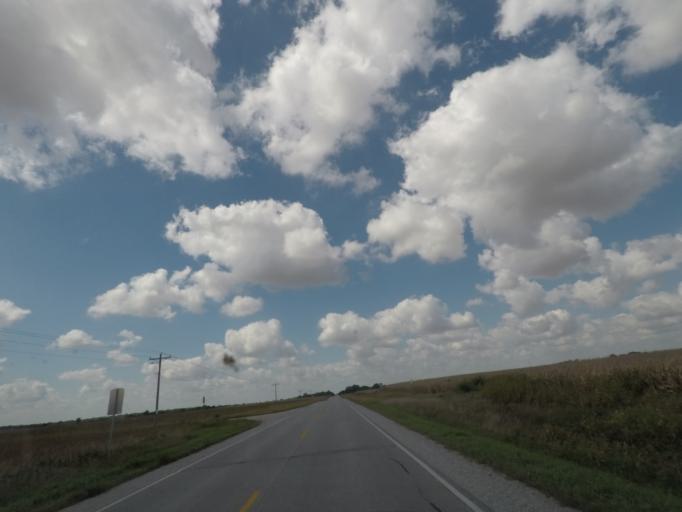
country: US
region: Iowa
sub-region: Story County
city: Nevada
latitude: 42.0226
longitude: -93.3566
